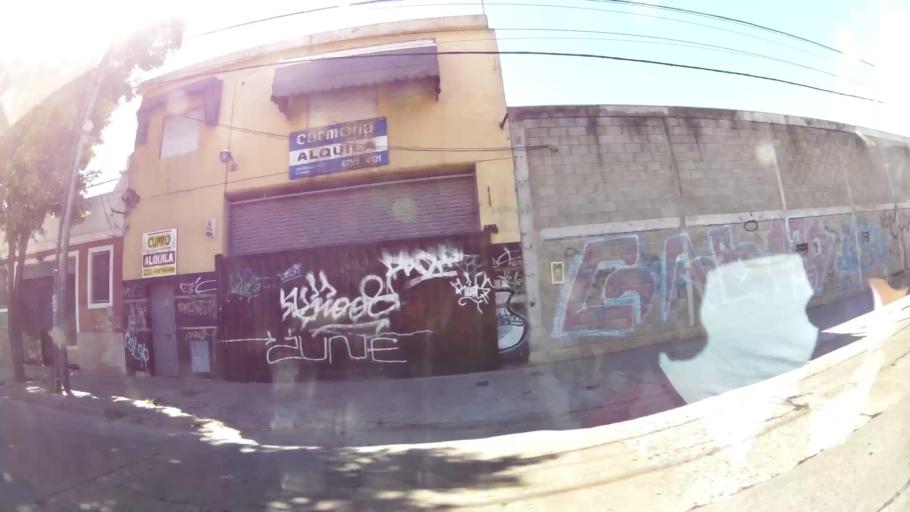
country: AR
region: Buenos Aires
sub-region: Partido de General San Martin
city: General San Martin
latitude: -34.5629
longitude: -58.5294
